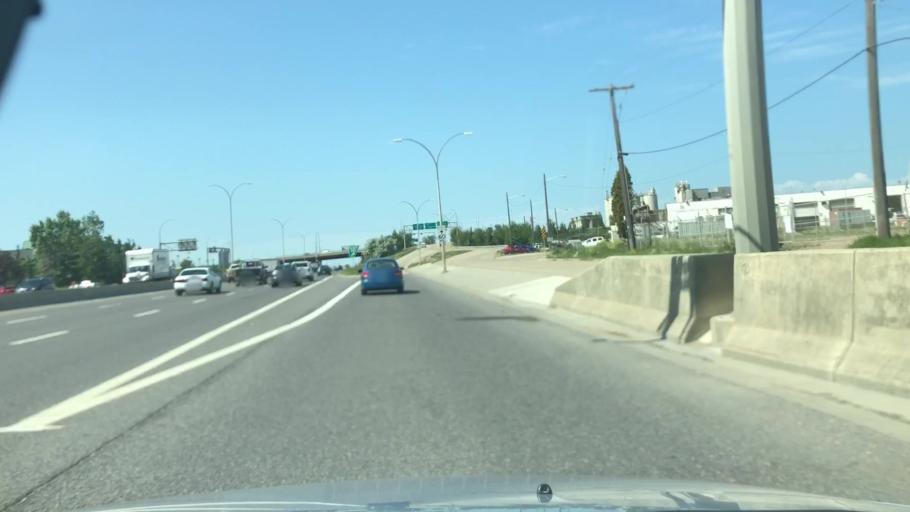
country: CA
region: Alberta
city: St. Albert
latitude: 53.5806
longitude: -113.5853
